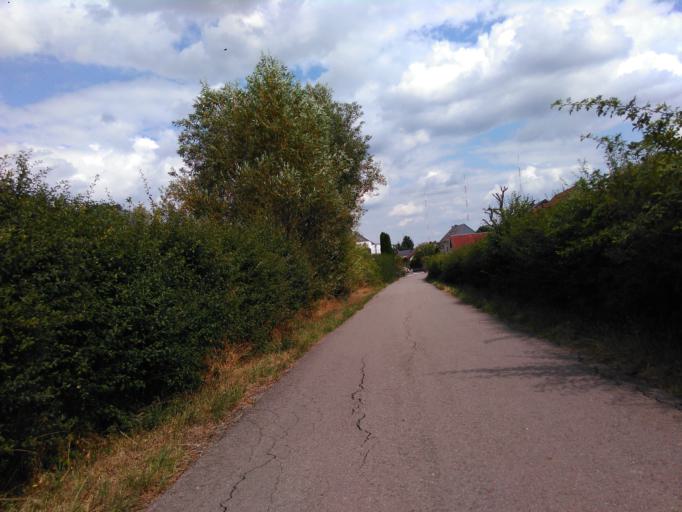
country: LU
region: Grevenmacher
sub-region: Canton de Grevenmacher
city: Junglinster
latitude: 49.7264
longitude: 6.2941
